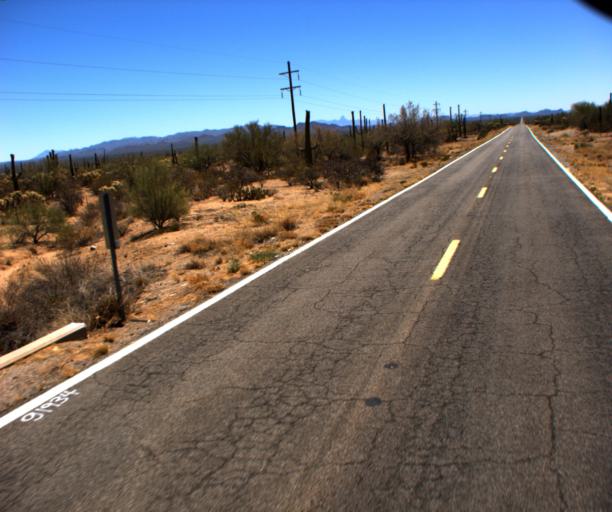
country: US
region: Arizona
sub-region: Pima County
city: Sells
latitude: 32.1118
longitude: -112.0750
